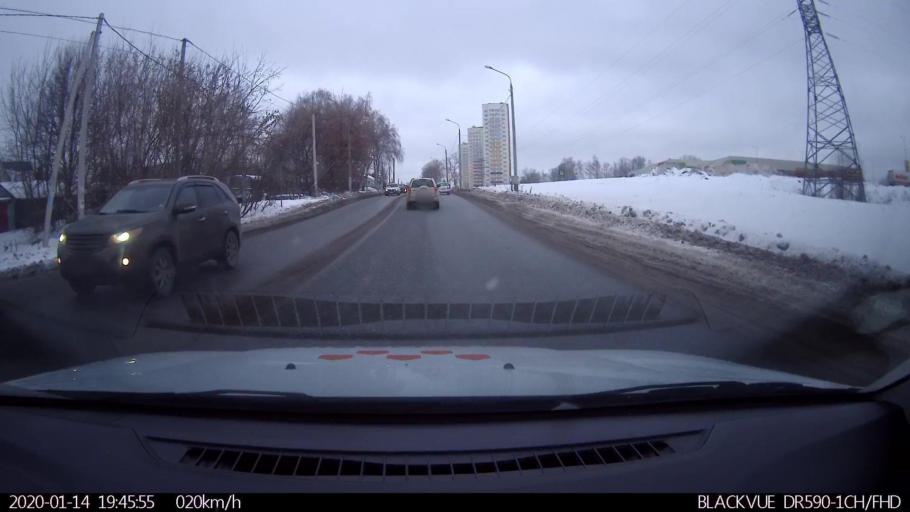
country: RU
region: Nizjnij Novgorod
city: Nizhniy Novgorod
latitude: 56.2572
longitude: 44.0089
